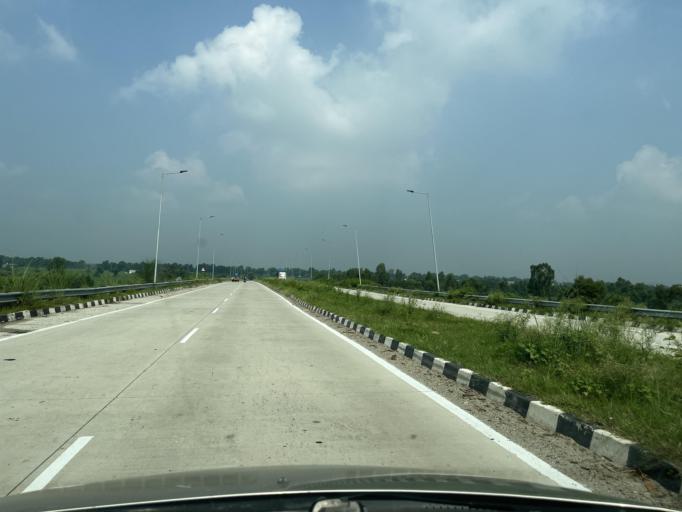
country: IN
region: Uttarakhand
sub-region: Udham Singh Nagar
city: Kashipur
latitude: 29.1744
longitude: 78.9446
